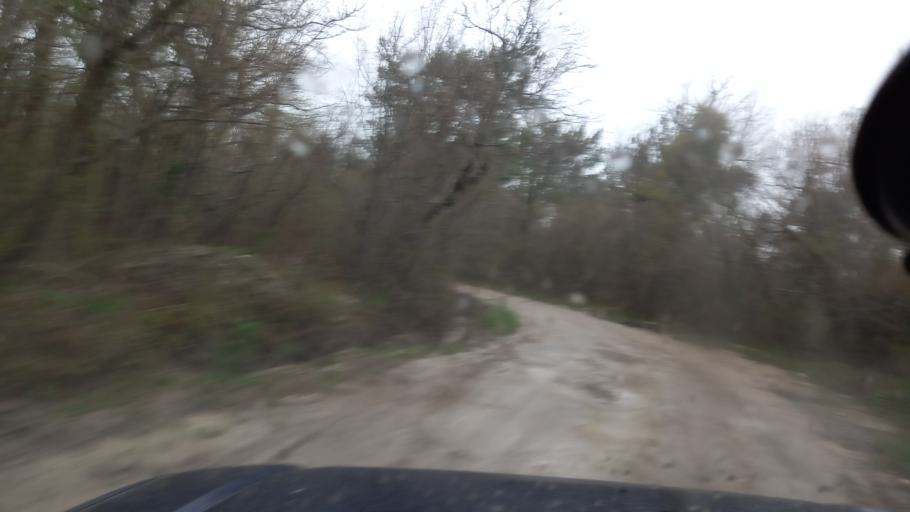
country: RU
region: Krasnodarskiy
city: Dzhubga
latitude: 44.3177
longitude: 38.6878
